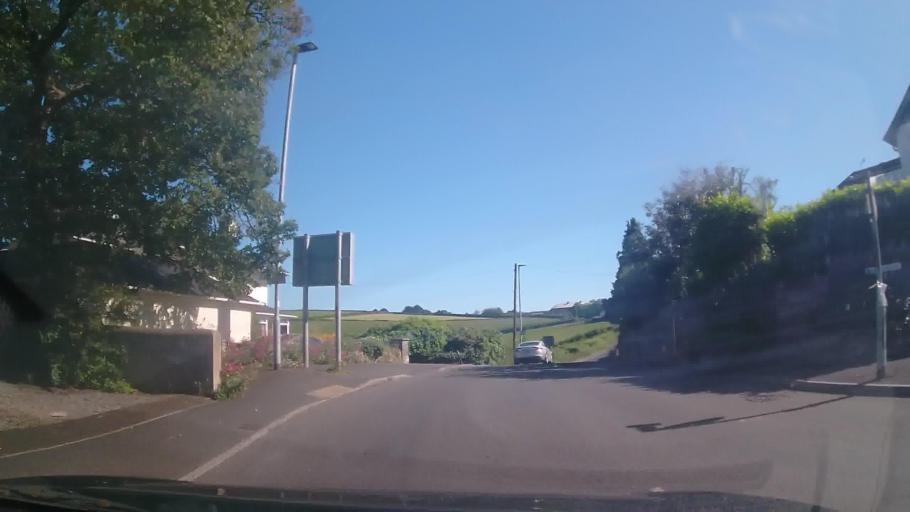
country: GB
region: England
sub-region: Devon
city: Dartmouth
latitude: 50.3499
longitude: -3.5931
